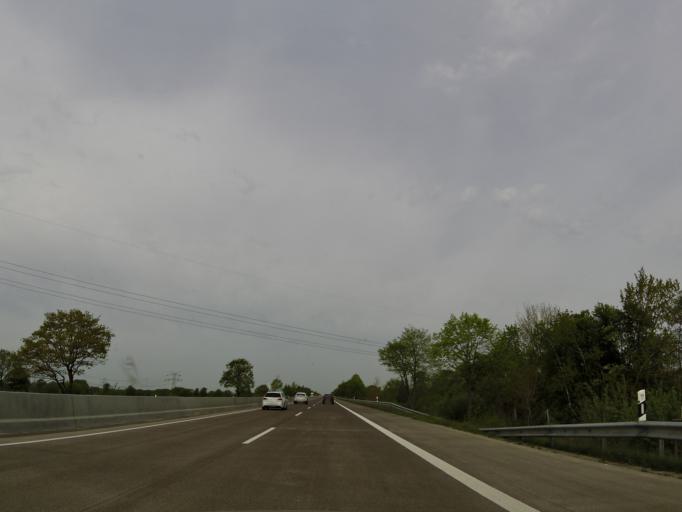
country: DE
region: Schleswig-Holstein
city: Horst
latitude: 53.8139
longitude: 9.6626
